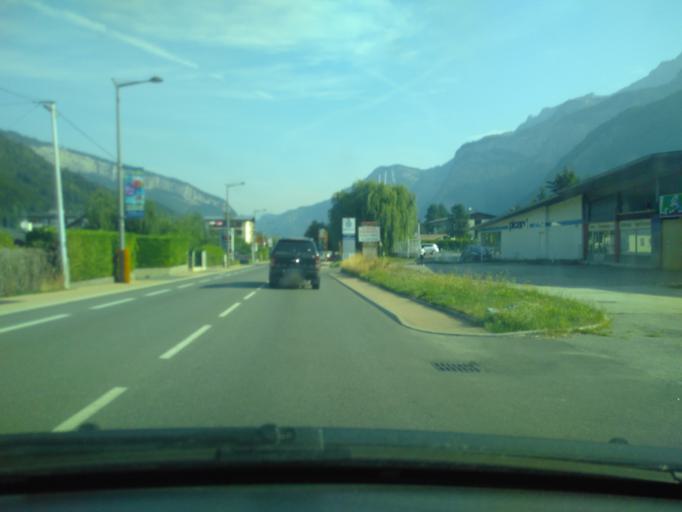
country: FR
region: Rhone-Alpes
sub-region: Departement de la Haute-Savoie
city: Sallanches
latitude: 45.9437
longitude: 6.6299
